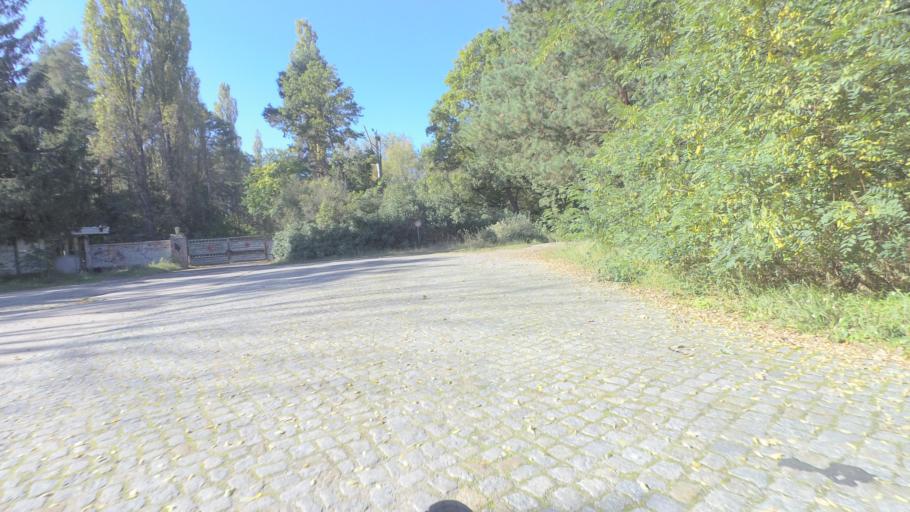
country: DE
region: Brandenburg
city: Sperenberg
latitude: 52.1428
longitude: 13.3531
